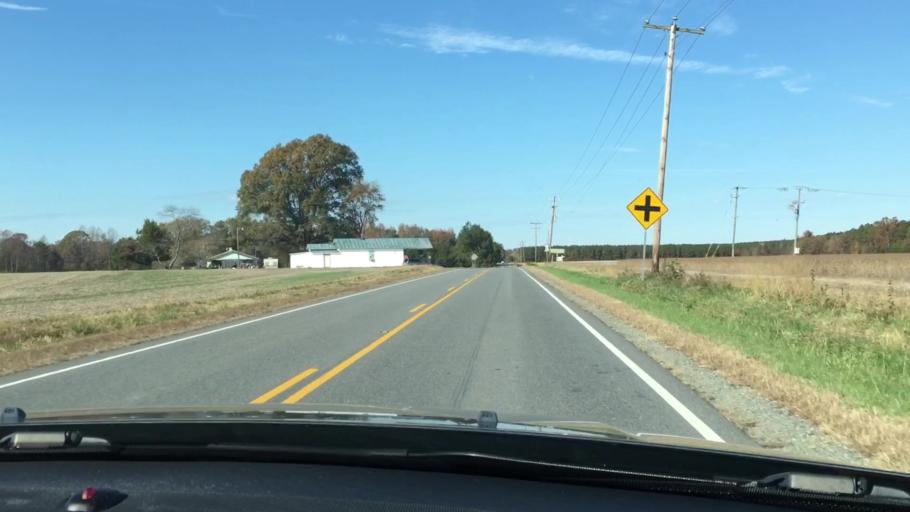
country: US
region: Virginia
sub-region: King and Queen County
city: King and Queen Court House
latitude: 37.6316
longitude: -76.9337
